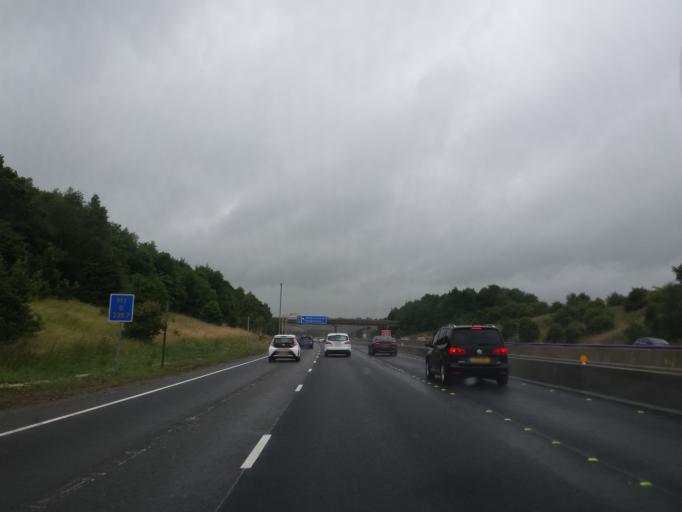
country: GB
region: England
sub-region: Derbyshire
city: Staveley
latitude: 53.2585
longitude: -1.3174
